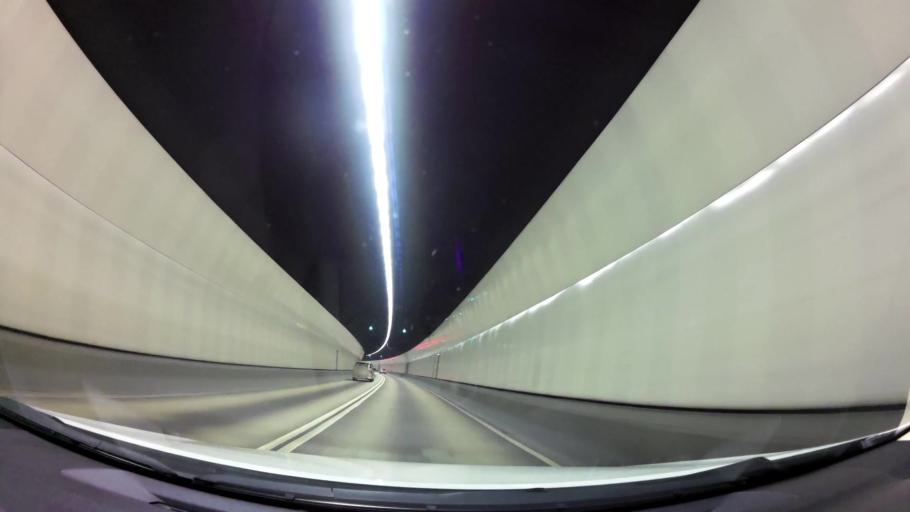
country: HK
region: Sha Tin
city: Sha Tin
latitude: 22.3778
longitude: 114.1448
